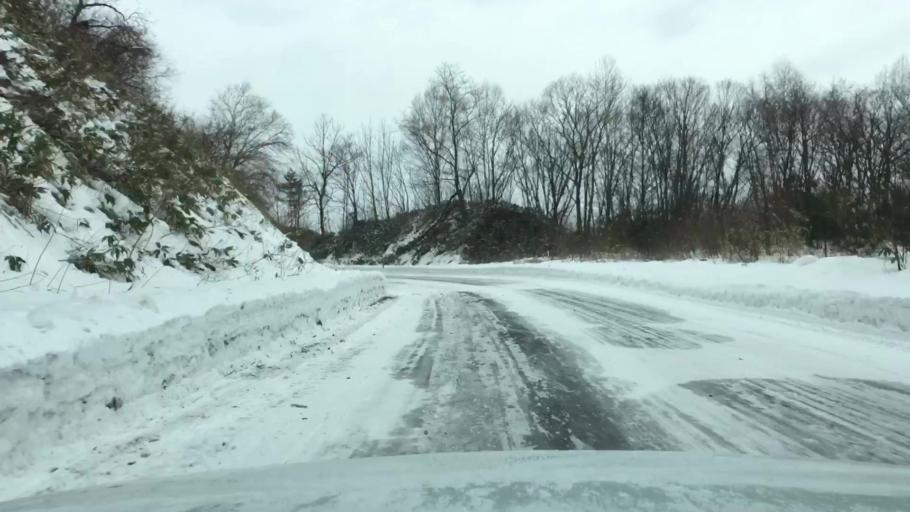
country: JP
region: Iwate
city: Shizukuishi
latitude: 39.9422
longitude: 140.9970
